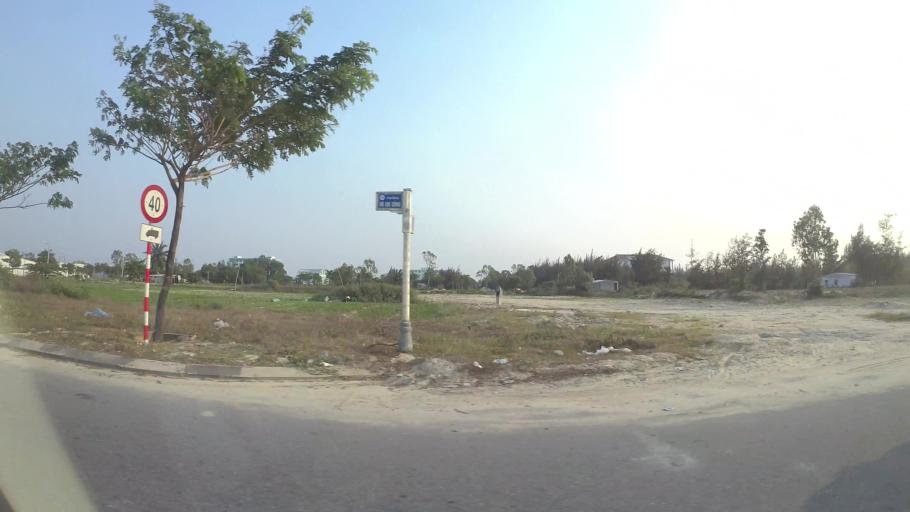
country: VN
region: Da Nang
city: Ngu Hanh Son
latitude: 15.9831
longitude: 108.2464
